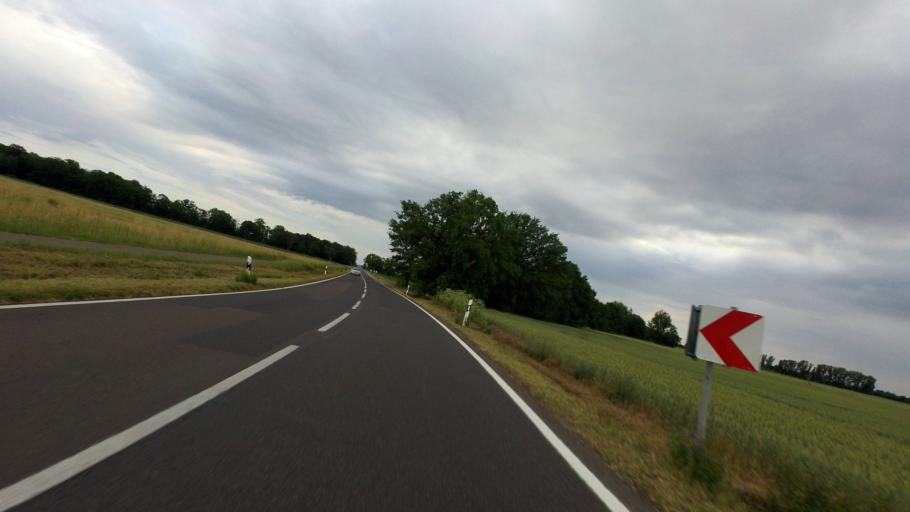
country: DE
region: Brandenburg
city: Pawesin
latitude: 52.4907
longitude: 12.6987
